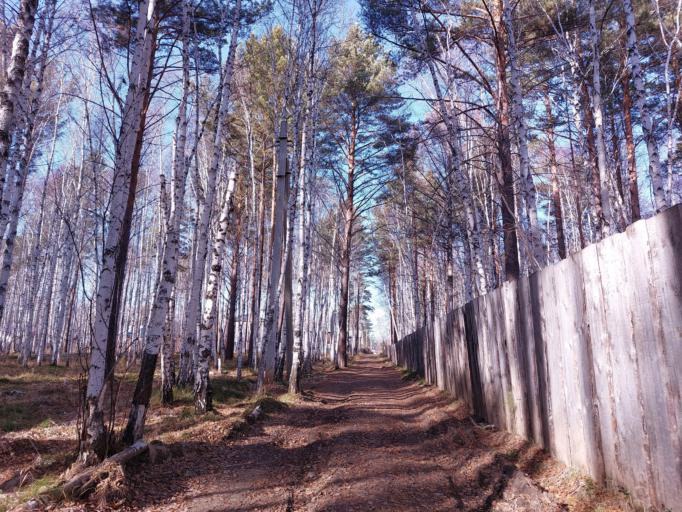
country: RU
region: Irkutsk
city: Pivovarikha
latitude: 52.1847
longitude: 104.4566
